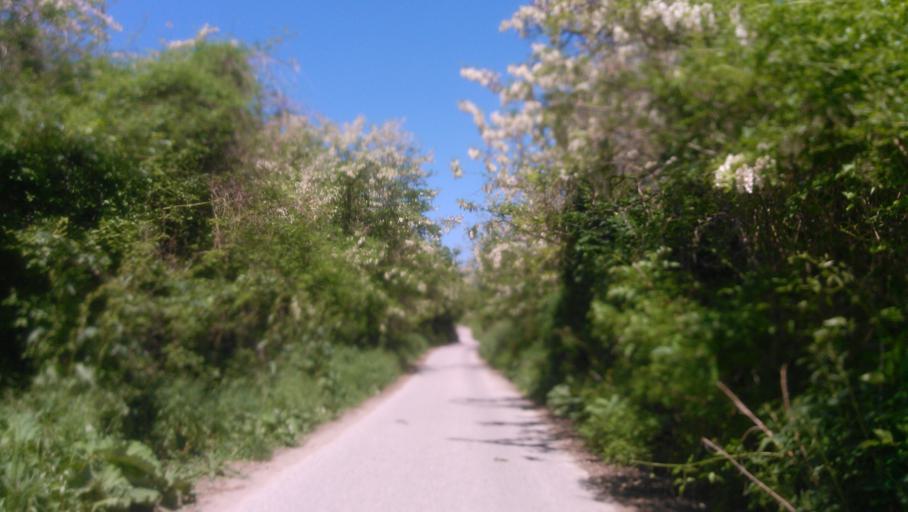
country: SK
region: Bratislavsky
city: Bratislava
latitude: 48.1793
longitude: 17.1219
